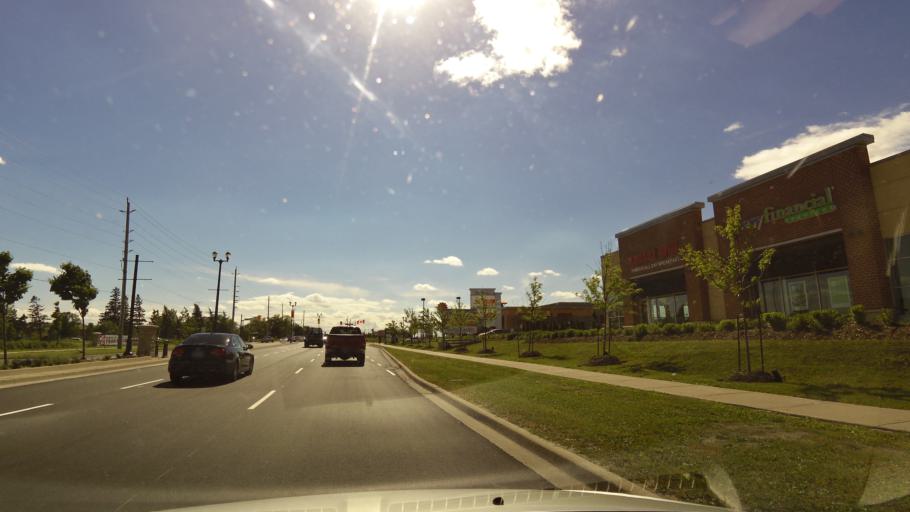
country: CA
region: Ontario
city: Bradford West Gwillimbury
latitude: 44.1081
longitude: -79.5925
